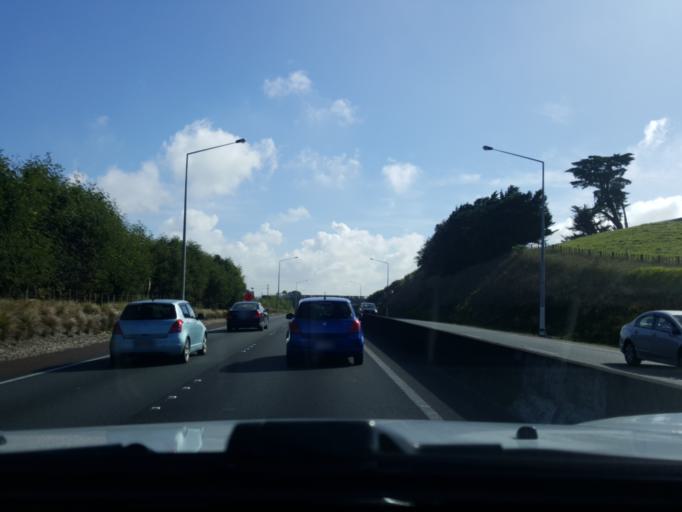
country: NZ
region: Auckland
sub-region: Auckland
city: Wiri
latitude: -36.9845
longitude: 174.8324
